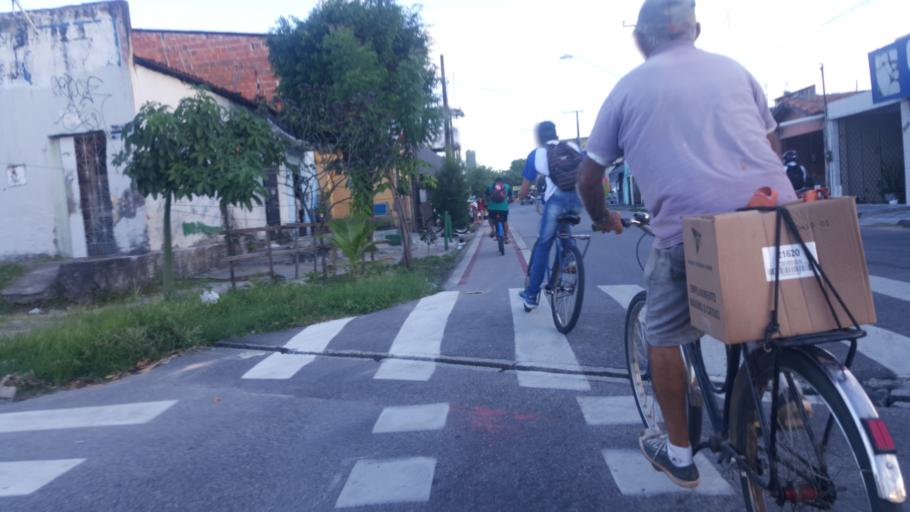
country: BR
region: Ceara
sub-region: Fortaleza
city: Fortaleza
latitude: -3.7525
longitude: -38.5400
